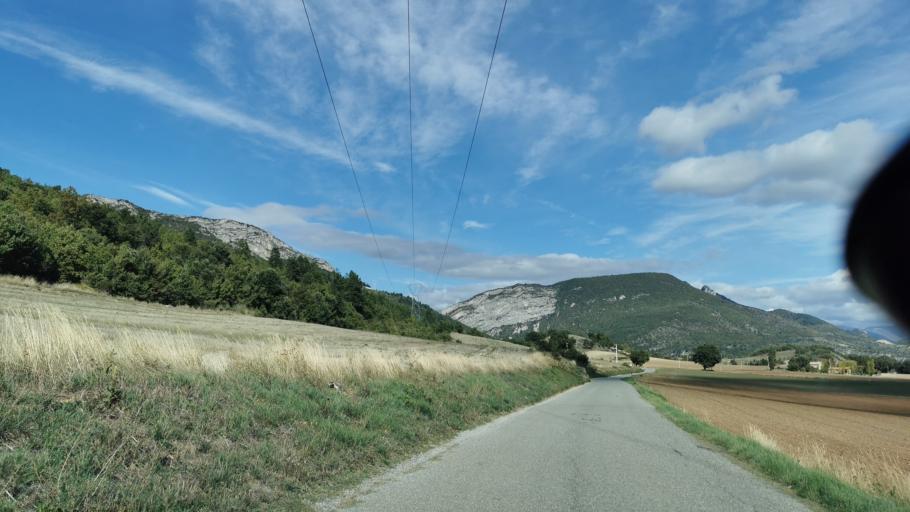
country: FR
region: Provence-Alpes-Cote d'Azur
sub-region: Departement des Alpes-de-Haute-Provence
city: Sisteron
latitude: 44.1762
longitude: 5.9736
